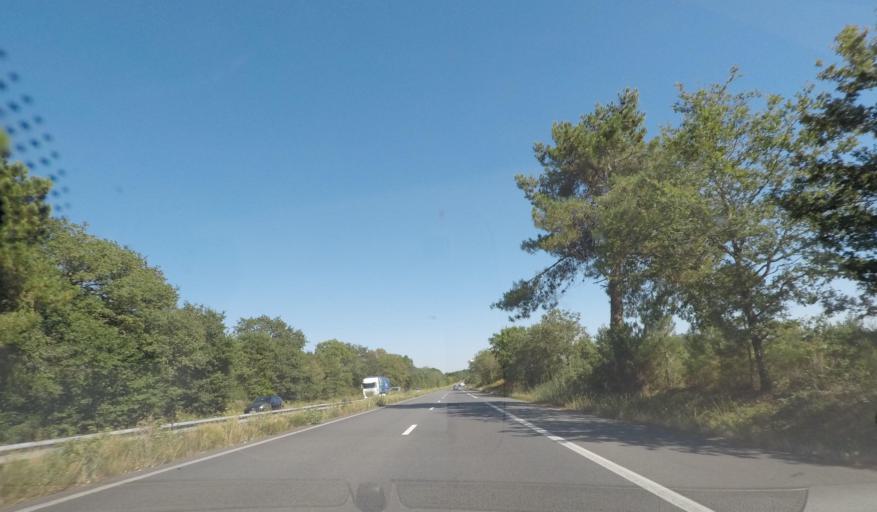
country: FR
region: Pays de la Loire
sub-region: Departement de la Loire-Atlantique
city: Missillac
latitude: 47.4835
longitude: -2.1965
